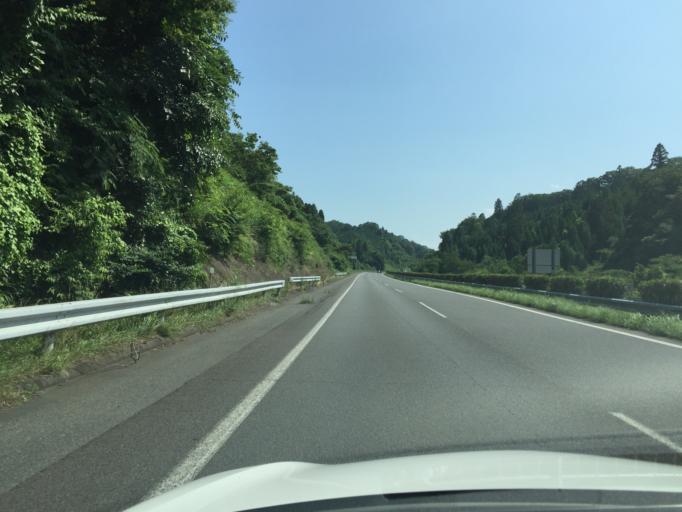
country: JP
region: Fukushima
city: Iwaki
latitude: 36.9953
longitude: 140.8061
